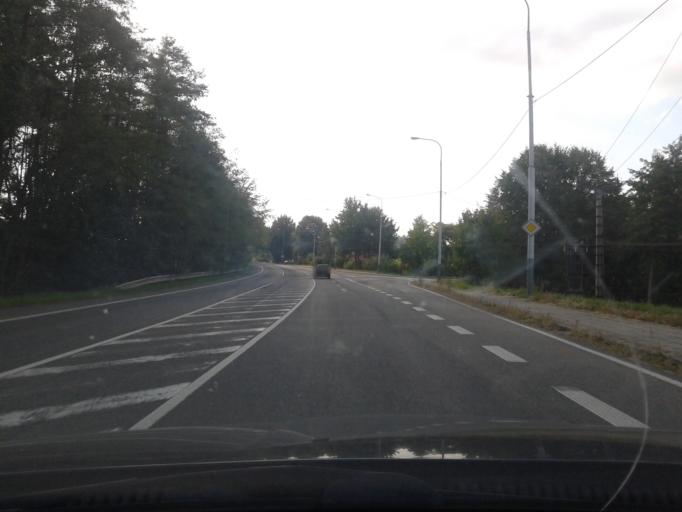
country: CZ
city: Dolni Lutyne
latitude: 49.9013
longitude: 18.4231
